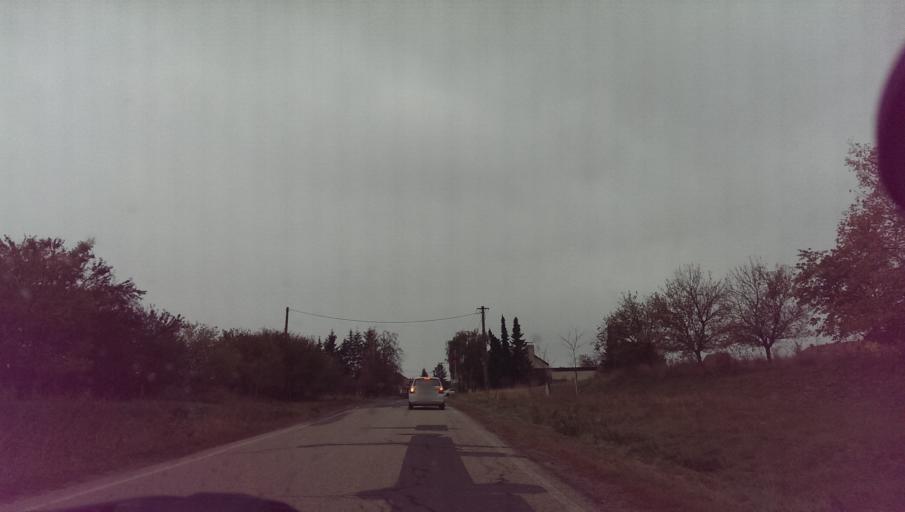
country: CZ
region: South Moravian
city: Orechov
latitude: 49.1204
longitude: 16.5262
